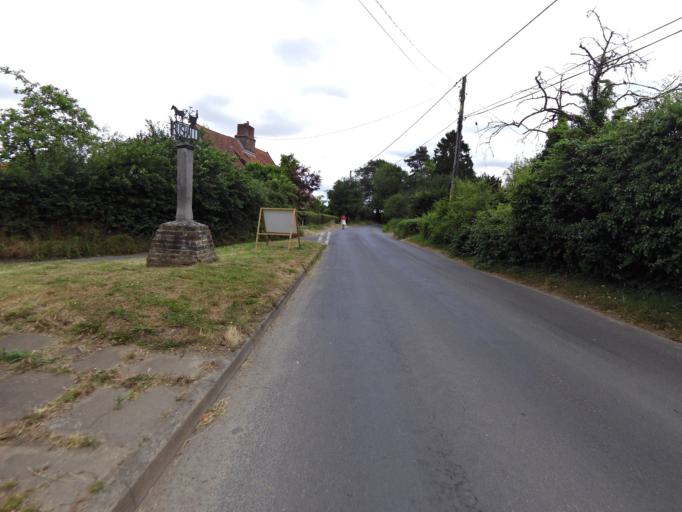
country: GB
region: England
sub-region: Norfolk
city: Harleston
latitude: 52.3989
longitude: 1.2317
